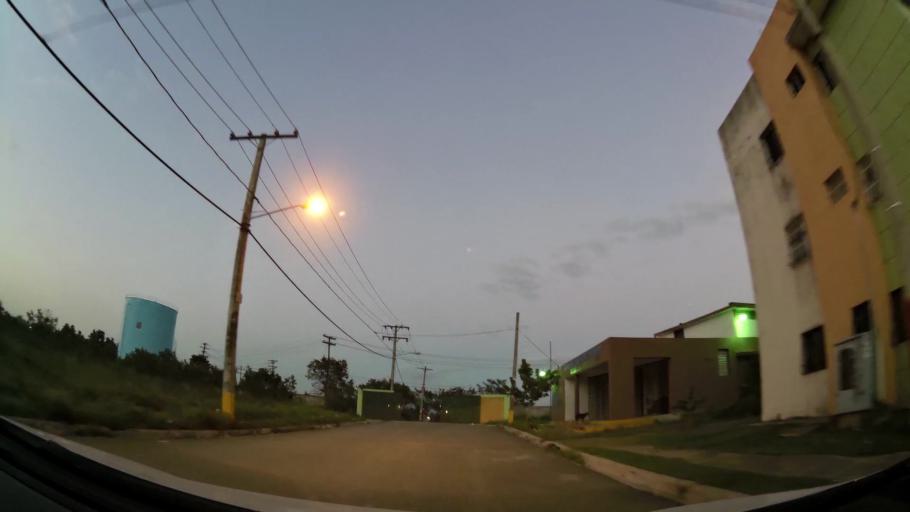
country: DO
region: Nacional
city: La Agustina
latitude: 18.5475
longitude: -69.9414
